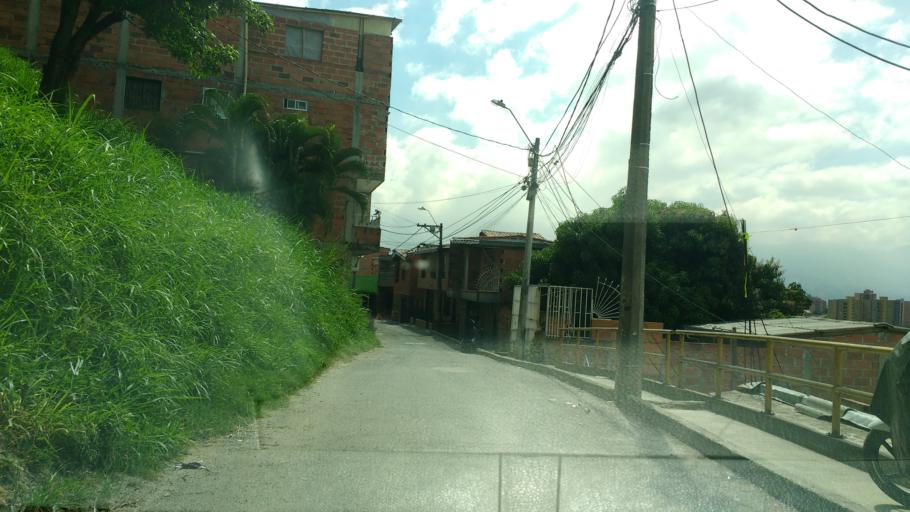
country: CO
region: Antioquia
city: Medellin
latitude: 6.2610
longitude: -75.6109
